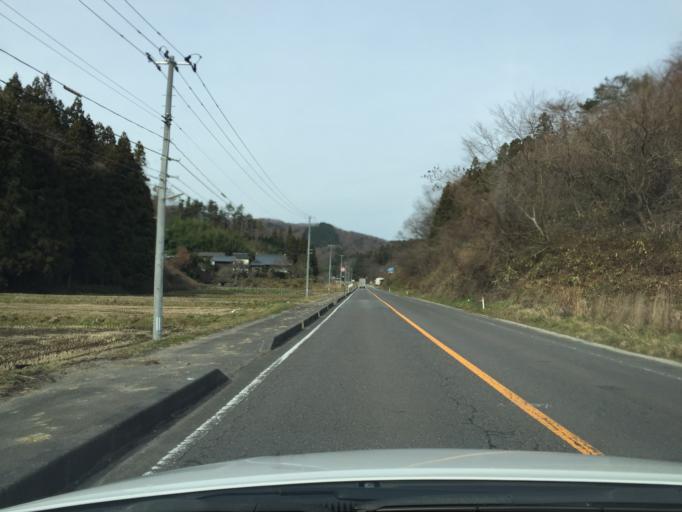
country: JP
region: Fukushima
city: Funehikimachi-funehiki
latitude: 37.3339
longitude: 140.6104
